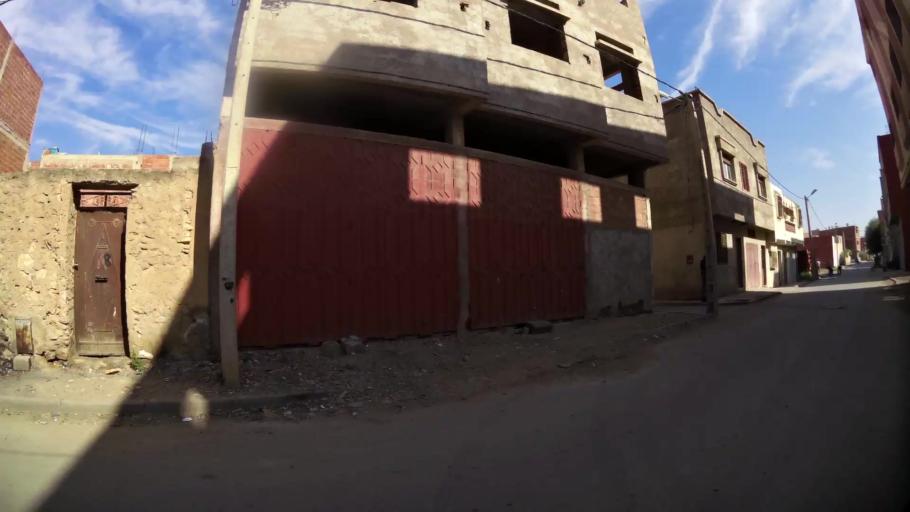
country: MA
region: Oriental
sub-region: Oujda-Angad
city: Oujda
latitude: 34.7202
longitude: -1.8837
